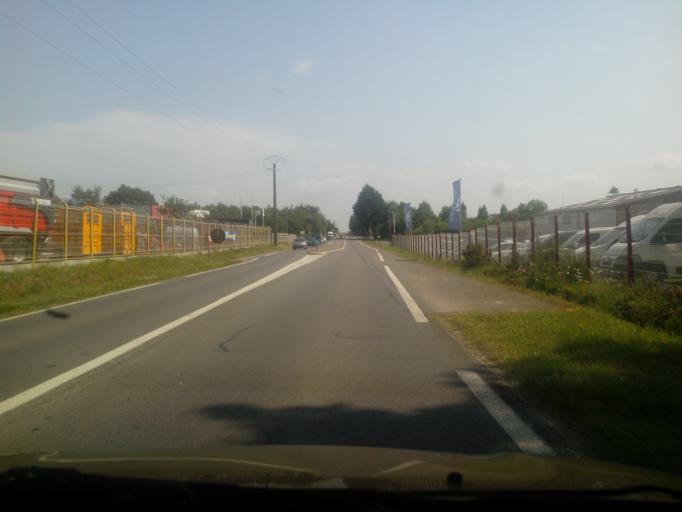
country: FR
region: Brittany
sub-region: Departement d'Ille-et-Vilaine
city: Melesse
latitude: 48.2289
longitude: -1.7060
